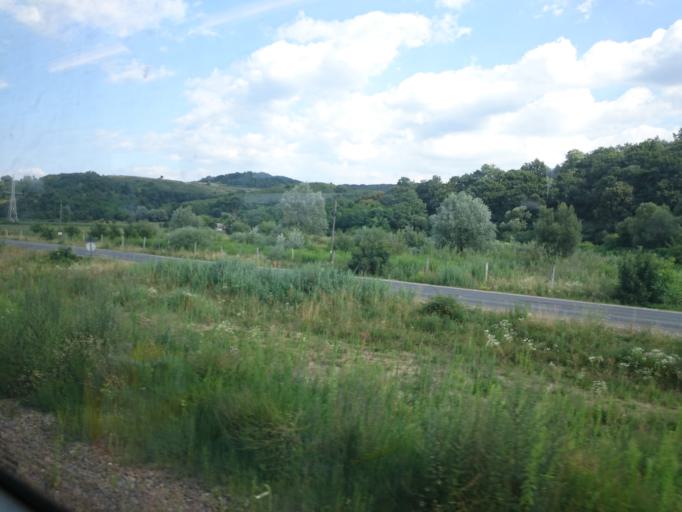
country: RO
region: Sibiu
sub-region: Comuna Hoghilag
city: Hoghilag
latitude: 46.2198
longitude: 24.6001
